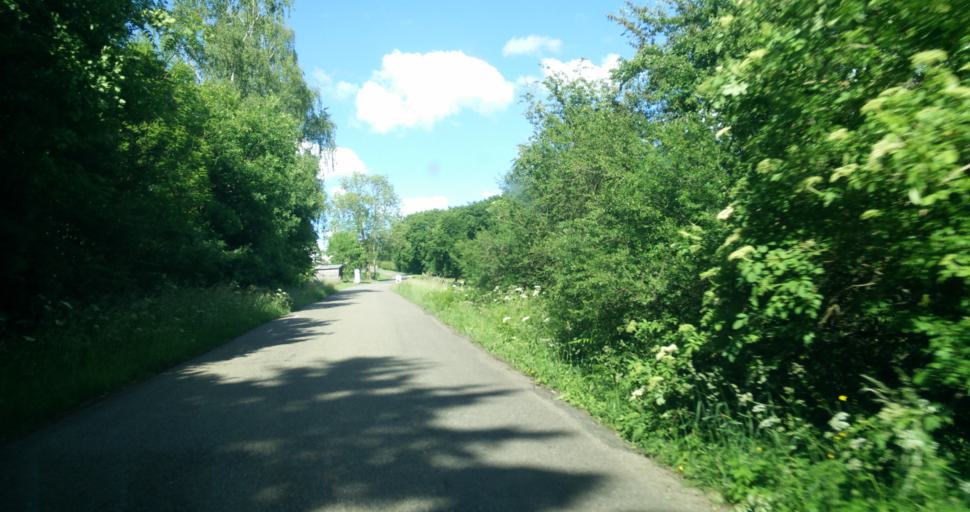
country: BE
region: Wallonia
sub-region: Province du Luxembourg
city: Houffalize
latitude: 50.1677
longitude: 5.7589
